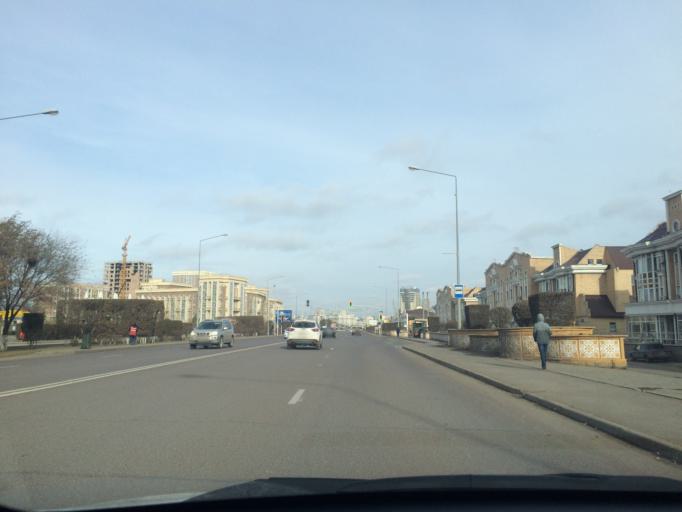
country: KZ
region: Astana Qalasy
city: Astana
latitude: 51.1379
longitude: 71.4167
